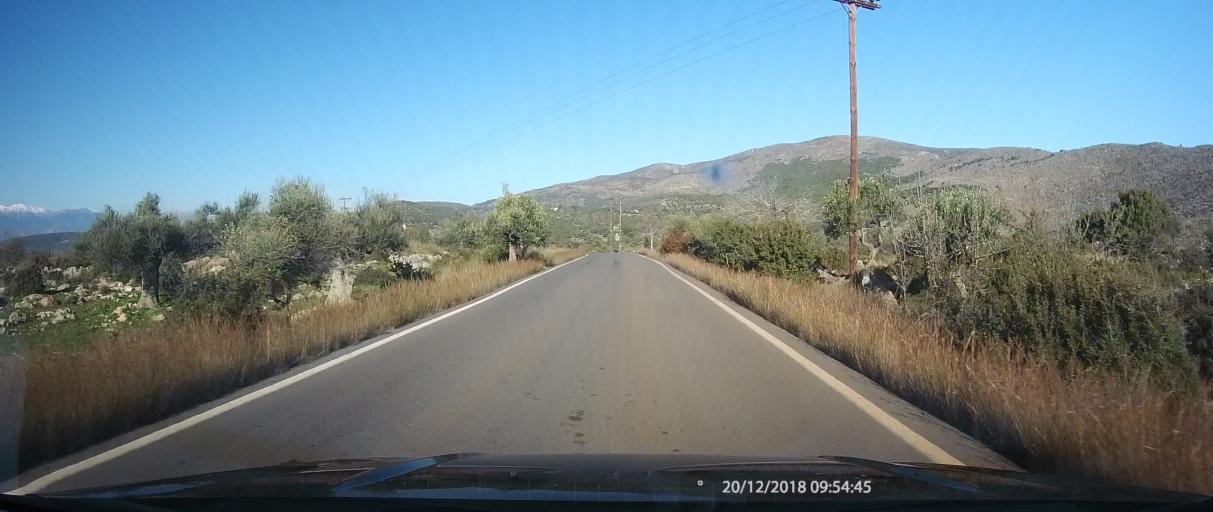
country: GR
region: Peloponnese
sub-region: Nomos Lakonias
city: Yerakion
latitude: 37.0196
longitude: 22.6315
